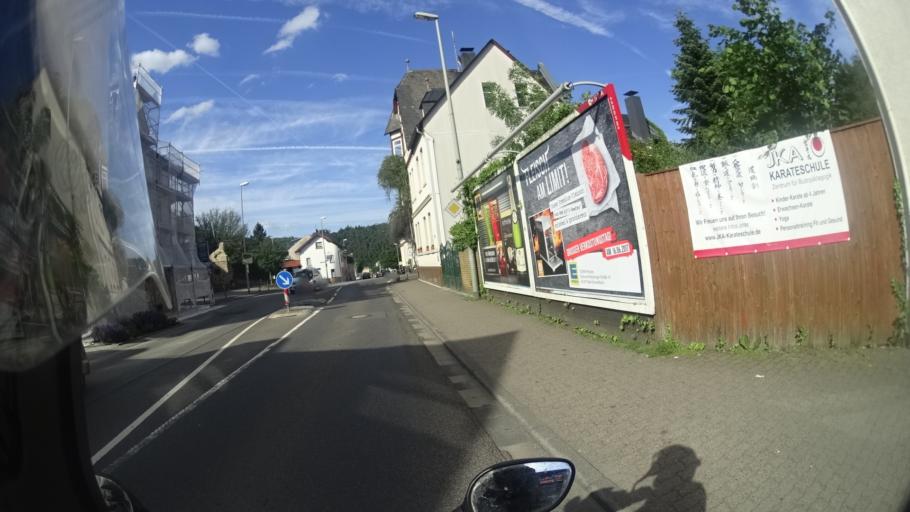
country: DE
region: Hesse
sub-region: Regierungsbezirk Darmstadt
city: Bad Schwalbach
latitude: 50.1452
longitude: 8.0767
